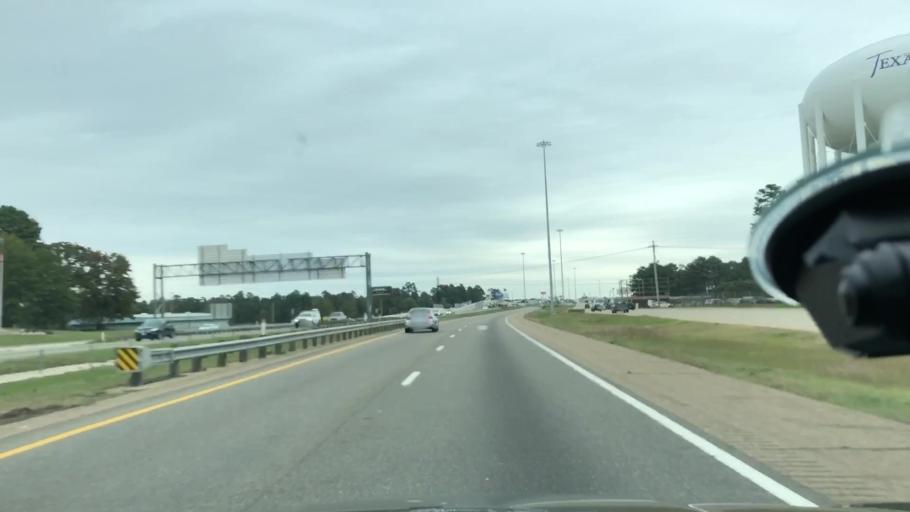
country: US
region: Arkansas
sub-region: Miller County
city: Texarkana
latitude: 33.4693
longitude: -94.0555
